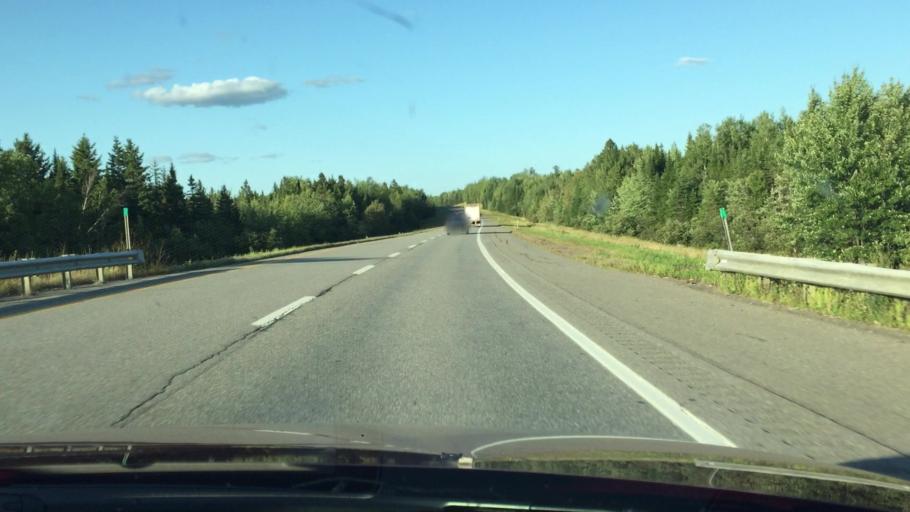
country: US
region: Maine
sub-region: Penobscot County
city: Patten
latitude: 46.0257
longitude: -68.2848
